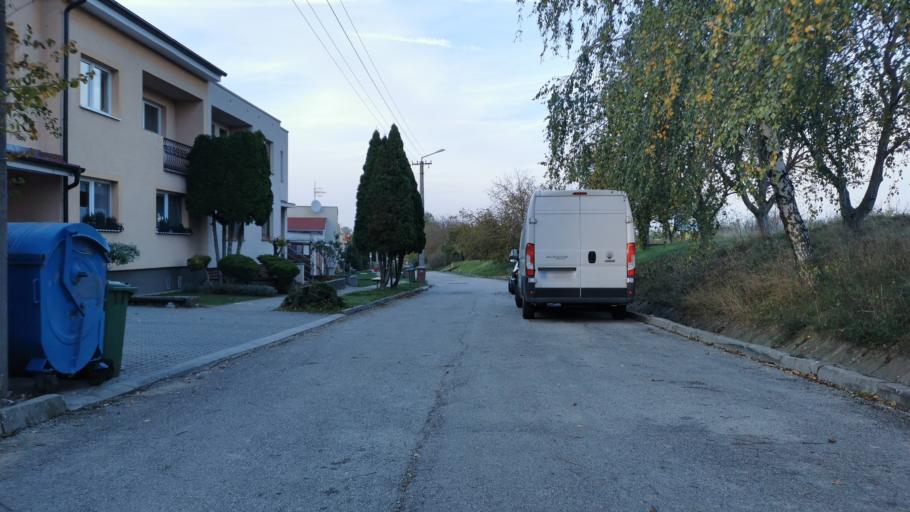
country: SK
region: Trnavsky
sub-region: Okres Skalica
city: Skalica
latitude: 48.8395
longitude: 17.2393
